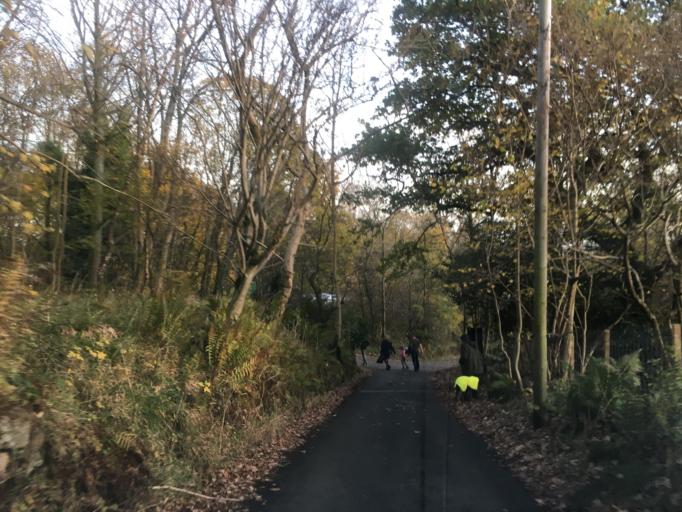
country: GB
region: Scotland
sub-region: Clackmannanshire
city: Dollar
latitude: 56.1722
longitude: -3.6717
